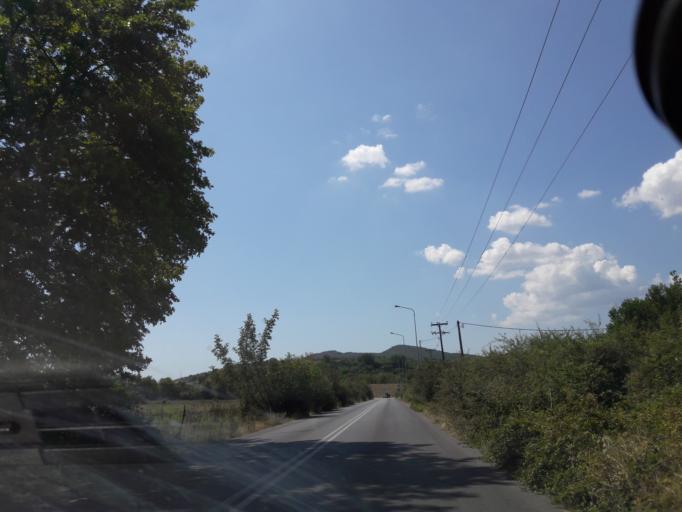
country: GR
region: Central Macedonia
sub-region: Nomos Chalkidikis
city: Megali Panagia
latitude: 40.3700
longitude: 23.6927
